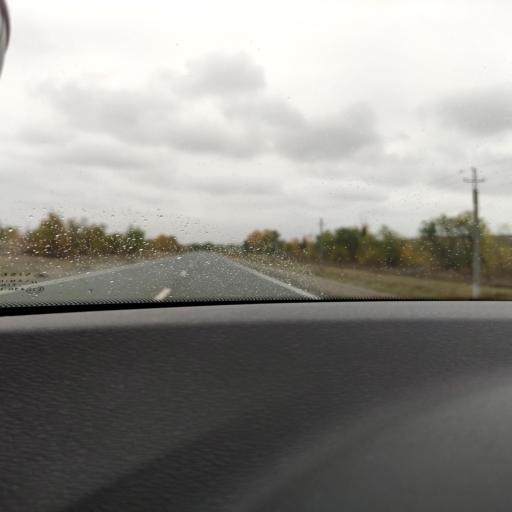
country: RU
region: Samara
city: Mirnyy
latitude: 53.6132
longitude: 50.2629
